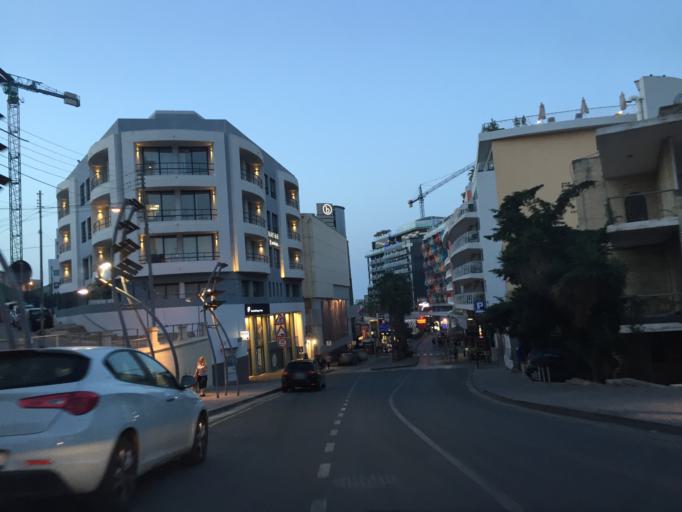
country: MT
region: Saint Julian
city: San Giljan
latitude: 35.9230
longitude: 14.4869
